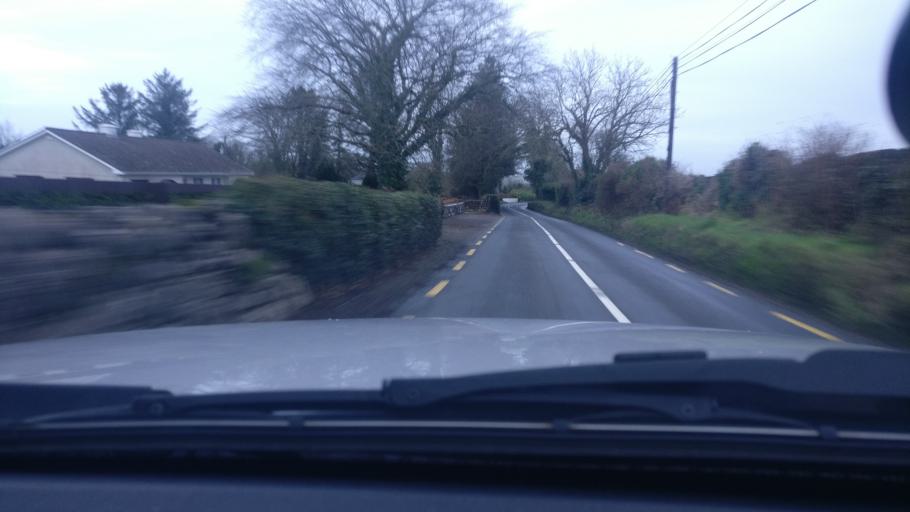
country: IE
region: Connaught
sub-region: County Galway
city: Loughrea
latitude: 53.1614
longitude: -8.5159
